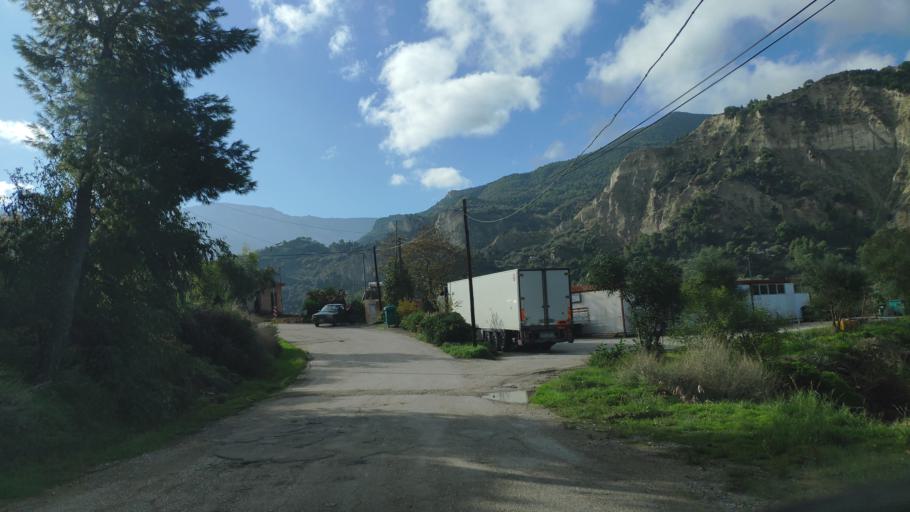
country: GR
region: West Greece
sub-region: Nomos Achaias
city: Aiyira
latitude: 38.1233
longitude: 22.4354
